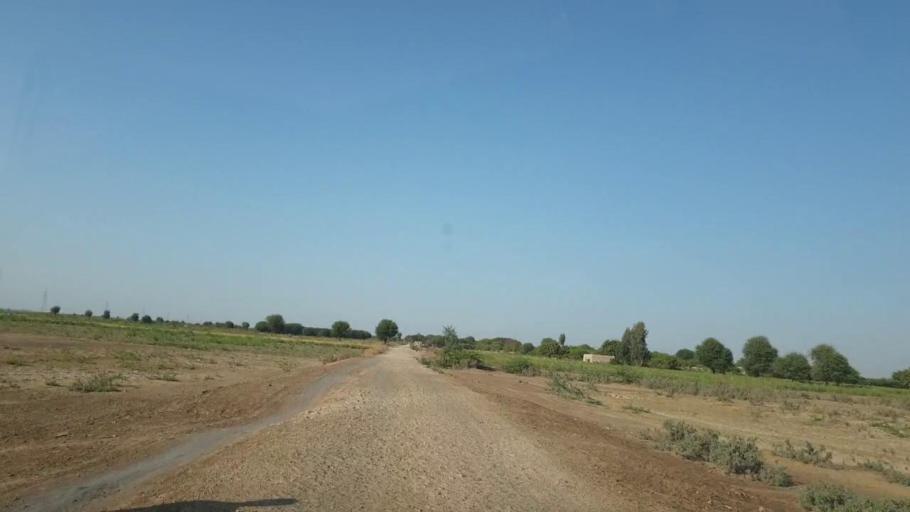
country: PK
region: Sindh
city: Kunri
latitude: 25.0452
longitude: 69.4420
